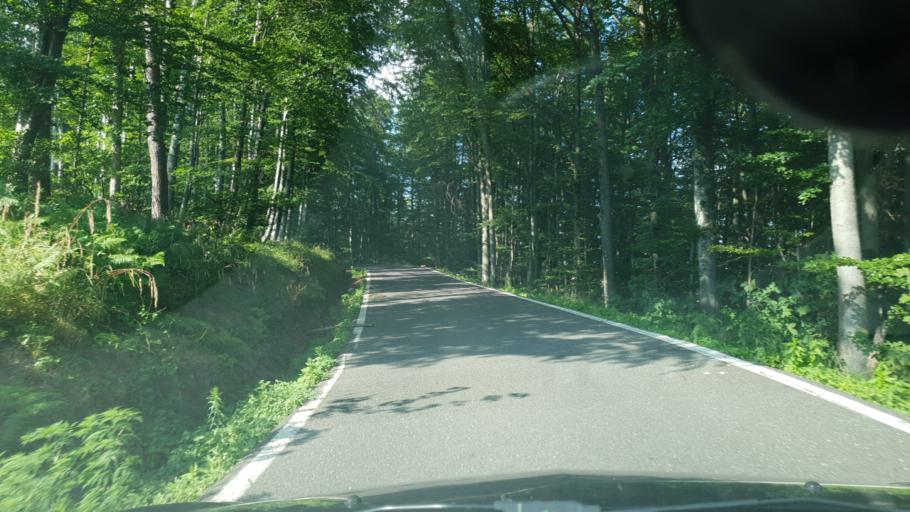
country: HR
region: Grad Zagreb
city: Kasina
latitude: 45.8845
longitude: 15.9704
